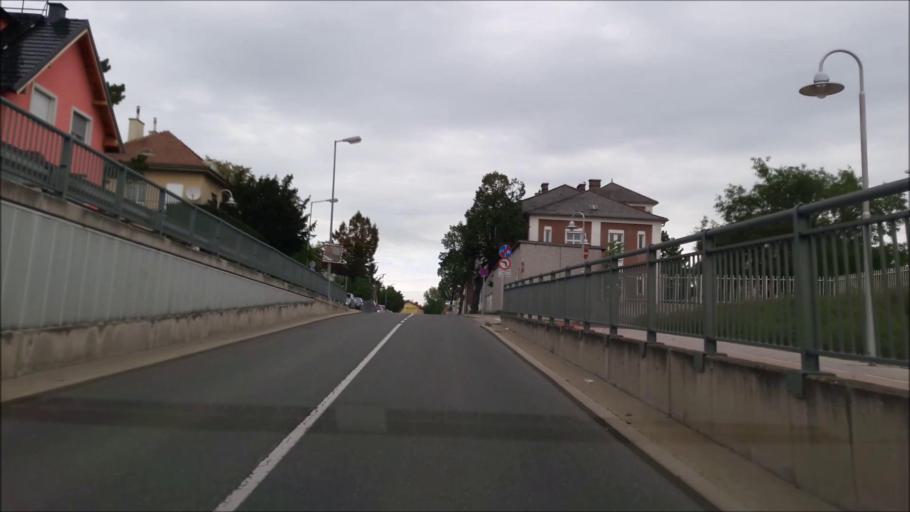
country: AT
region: Lower Austria
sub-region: Politischer Bezirk Wien-Umgebung
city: Schwechat
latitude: 48.1459
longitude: 16.4795
